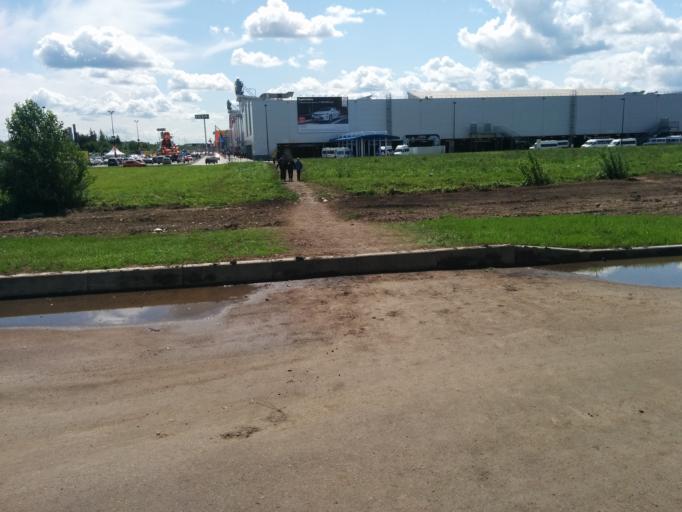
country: RU
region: Bashkortostan
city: Ufa
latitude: 54.6779
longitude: 55.9309
